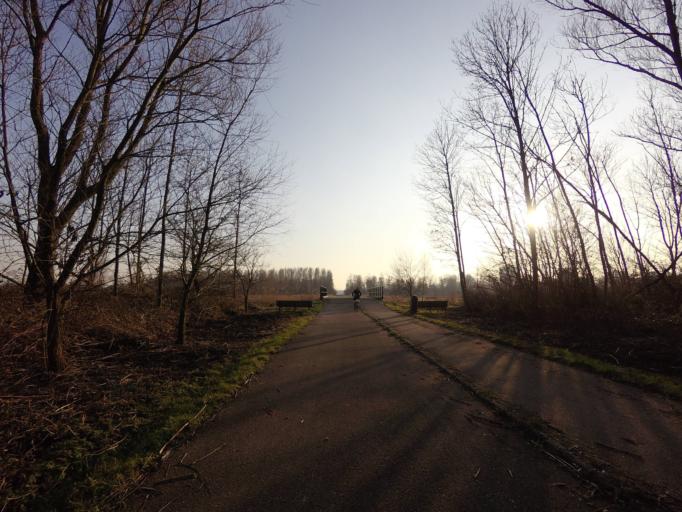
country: NL
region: North Holland
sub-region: Gemeente Haarlem
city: Haarlem
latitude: 52.3646
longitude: 4.6721
